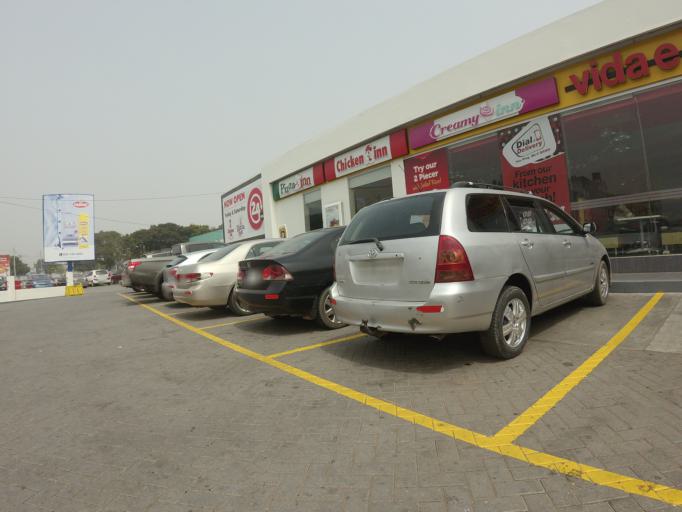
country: GH
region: Greater Accra
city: Accra
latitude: 5.6044
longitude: -0.1754
